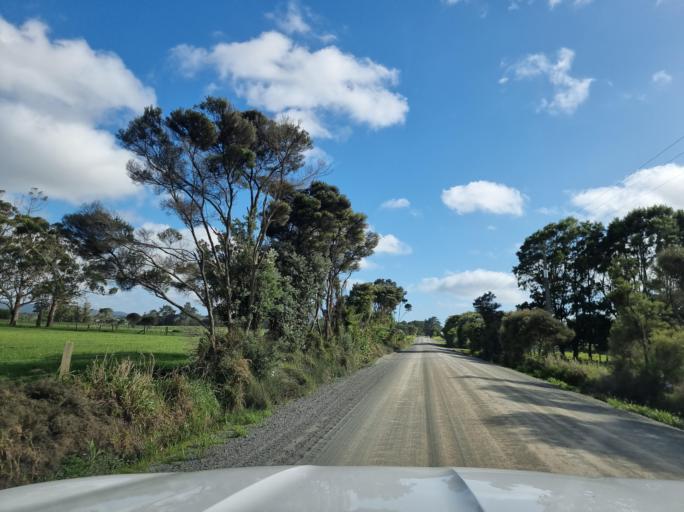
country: NZ
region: Auckland
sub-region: Auckland
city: Wellsford
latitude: -36.1314
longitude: 174.5924
